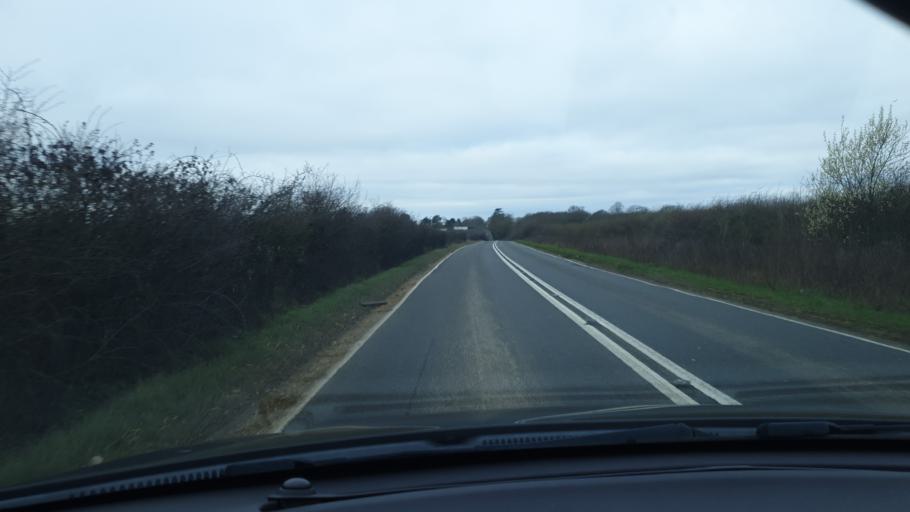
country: GB
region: England
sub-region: Essex
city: Little Clacton
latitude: 51.8632
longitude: 1.1482
